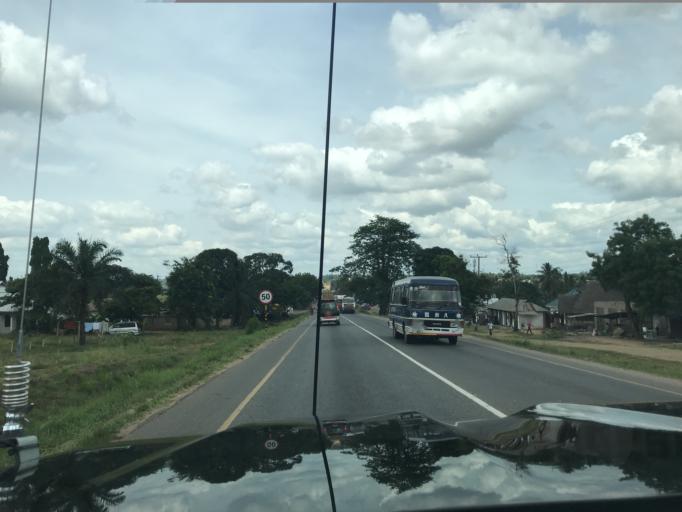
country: TZ
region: Pwani
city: Kibaha
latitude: -6.7655
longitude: 38.9557
